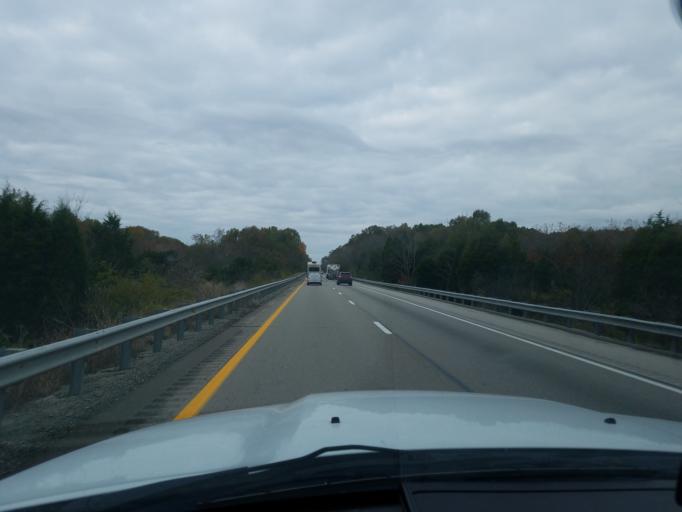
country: US
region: Indiana
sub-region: Switzerland County
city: Vevay
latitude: 38.6769
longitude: -84.9904
